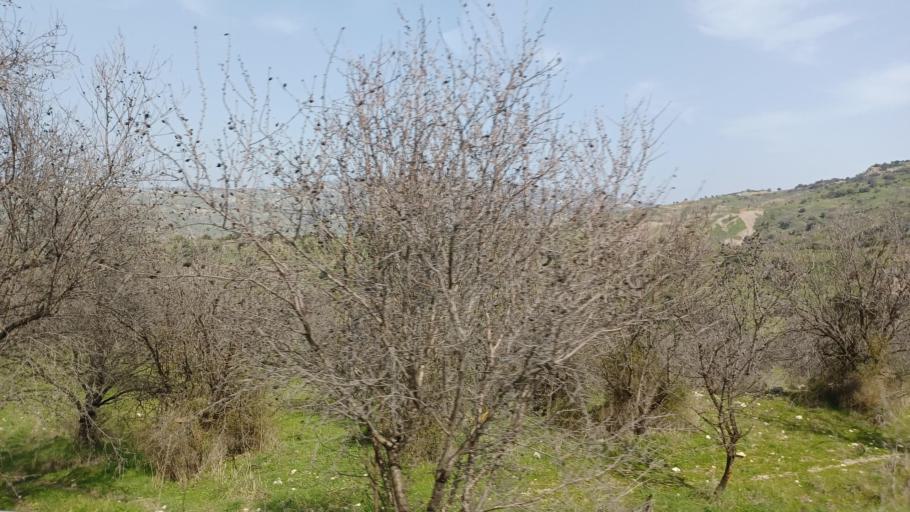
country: CY
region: Limassol
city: Pissouri
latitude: 34.7569
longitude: 32.6494
